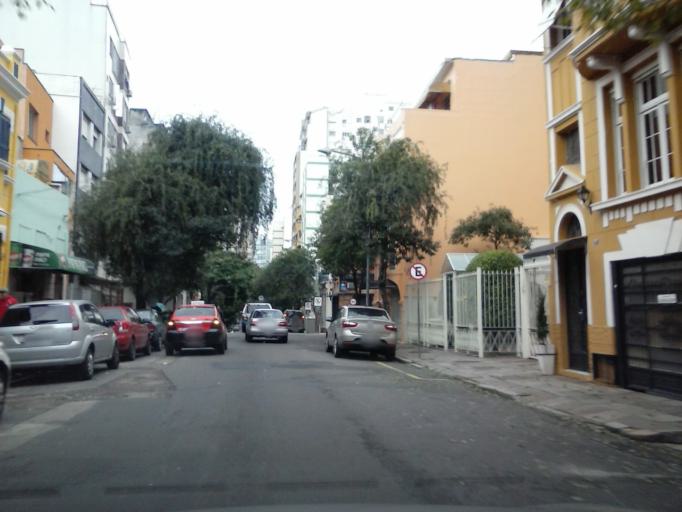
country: BR
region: Rio Grande do Sul
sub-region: Porto Alegre
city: Porto Alegre
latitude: -30.0341
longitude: -51.2359
